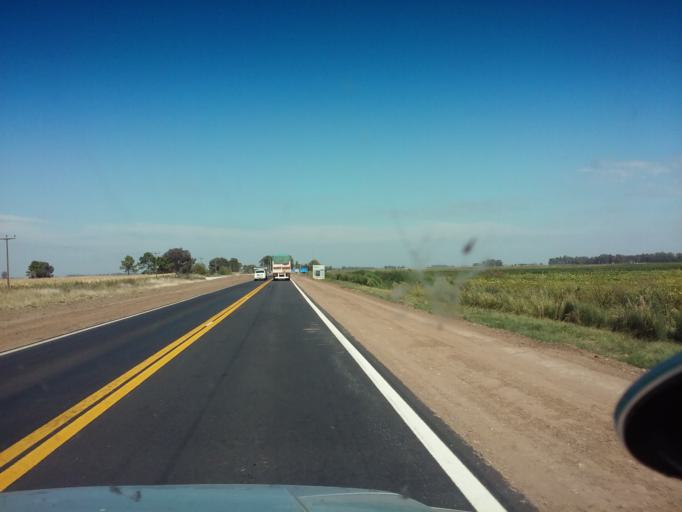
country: AR
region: Buenos Aires
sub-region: Partido de Nueve de Julio
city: Nueve de Julio
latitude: -35.3556
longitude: -60.6973
